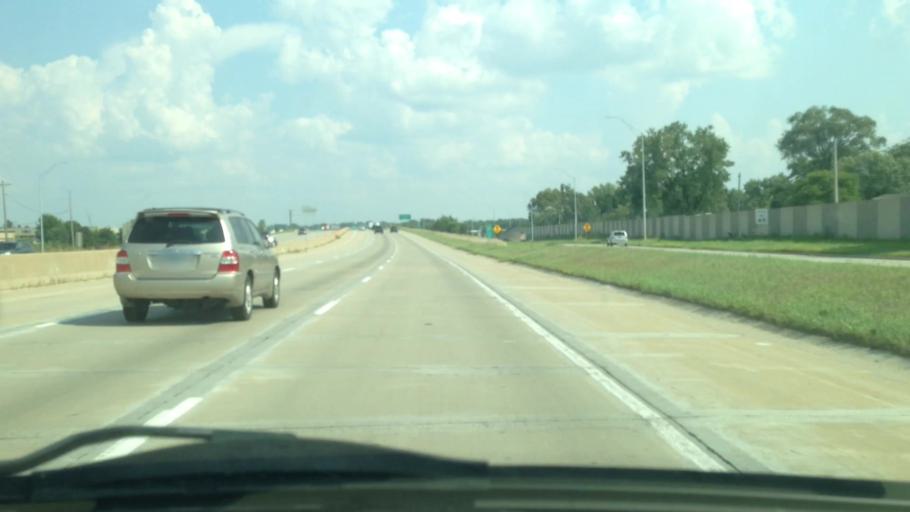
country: US
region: Iowa
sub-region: Black Hawk County
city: Waterloo
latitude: 42.5051
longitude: -92.3705
